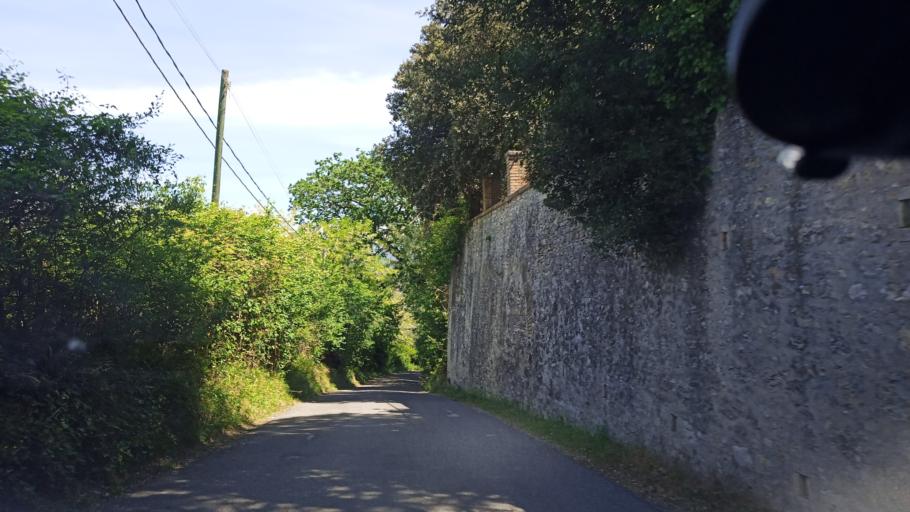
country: IT
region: Latium
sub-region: Provincia di Rieti
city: Torri in Sabina
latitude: 42.3540
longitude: 12.6319
